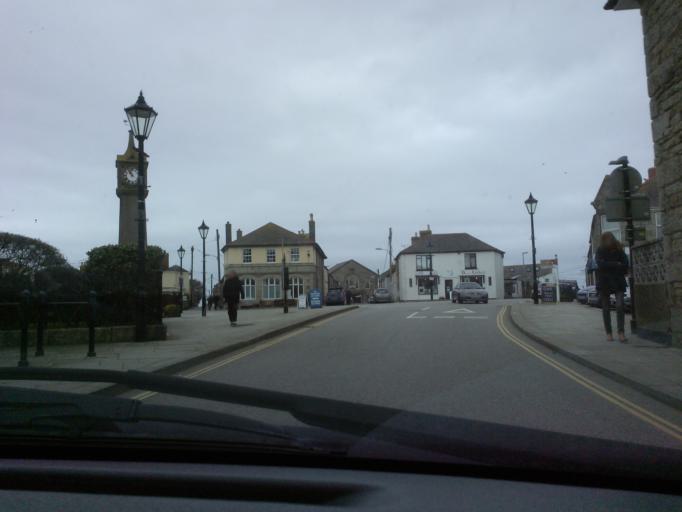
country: GB
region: England
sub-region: Cornwall
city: Saint Just
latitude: 50.1245
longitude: -5.6801
